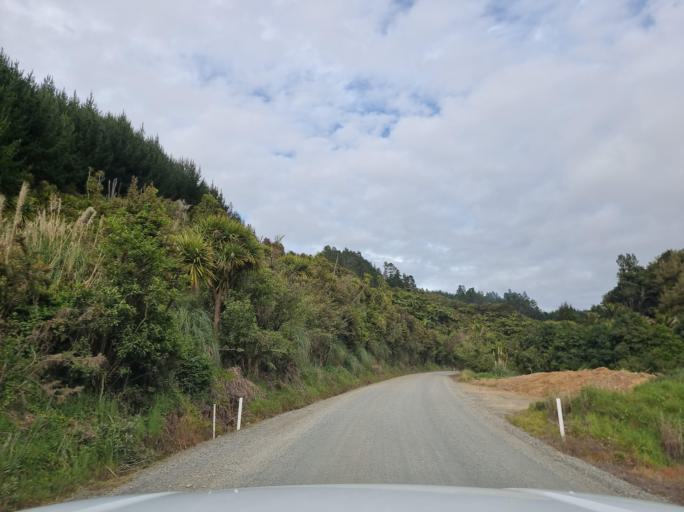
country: NZ
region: Northland
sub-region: Whangarei
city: Ruakaka
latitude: -36.0527
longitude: 174.4031
